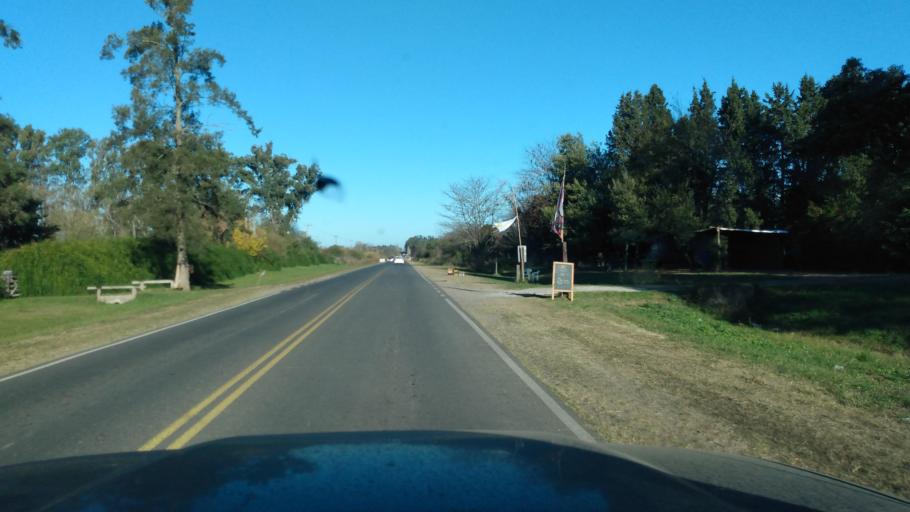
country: AR
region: Buenos Aires
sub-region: Partido de Lujan
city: Lujan
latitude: -34.5194
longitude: -59.1766
